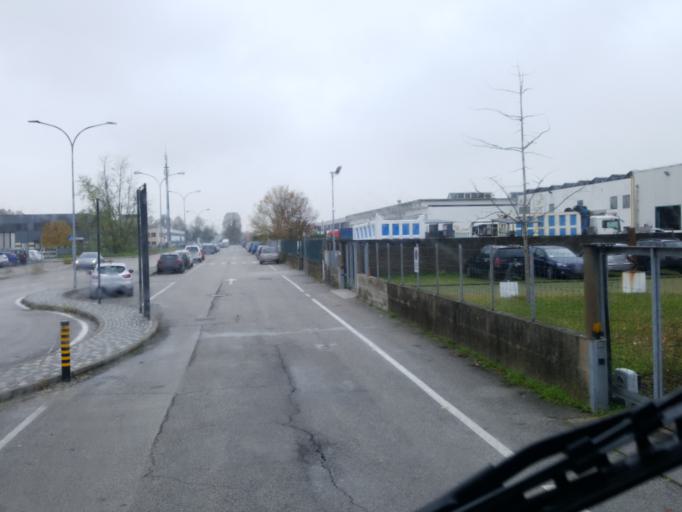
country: IT
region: Veneto
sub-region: Provincia di Treviso
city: Mogliano Veneto
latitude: 45.5545
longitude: 12.2268
